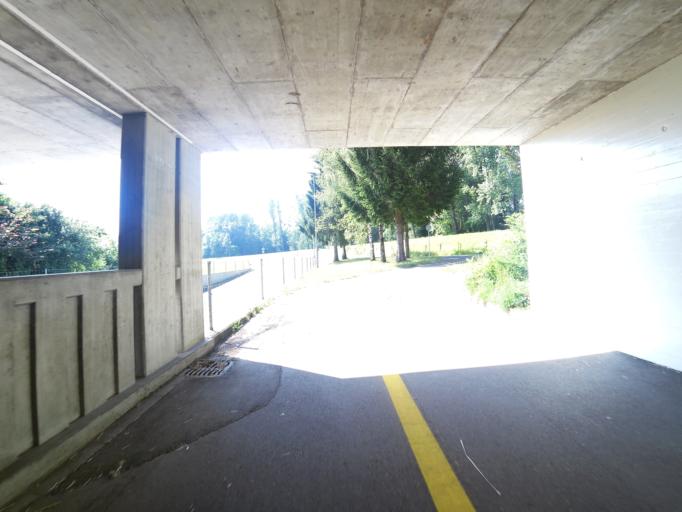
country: CH
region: Thurgau
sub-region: Weinfelden District
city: Wigoltingen
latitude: 47.5880
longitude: 9.0160
